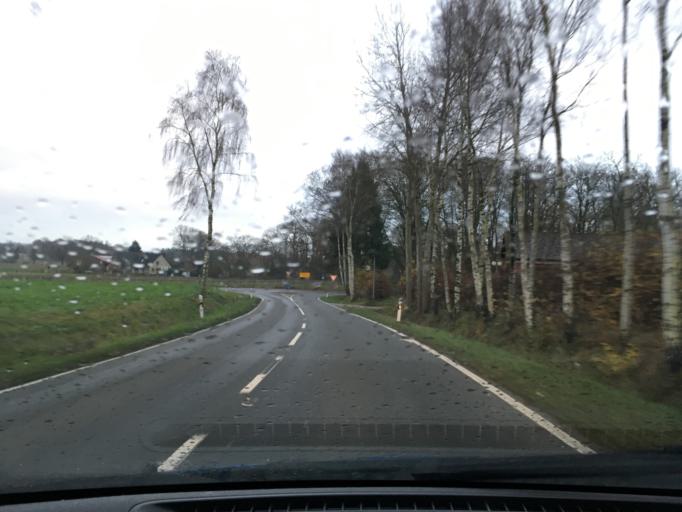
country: DE
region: Lower Saxony
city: Hermannsburg
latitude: 52.8183
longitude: 10.0589
